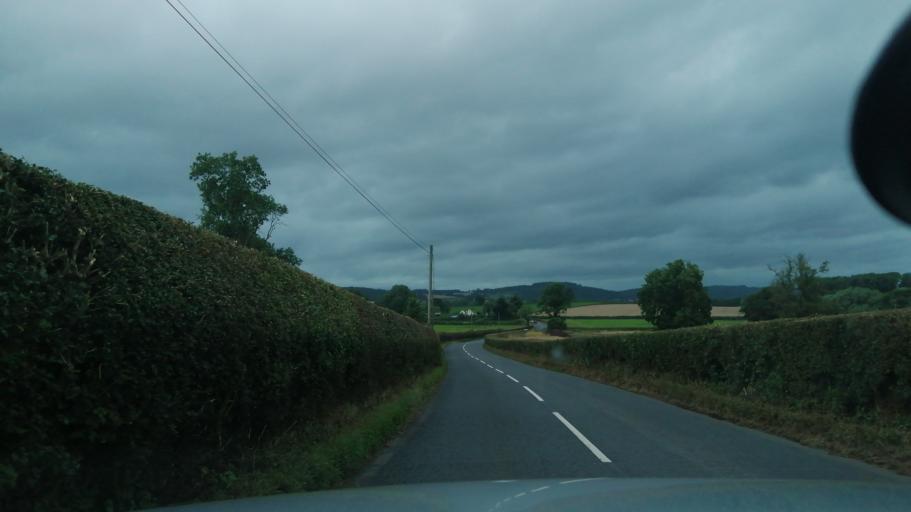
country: GB
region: England
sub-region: Herefordshire
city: Thruxton
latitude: 52.0085
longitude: -2.8216
